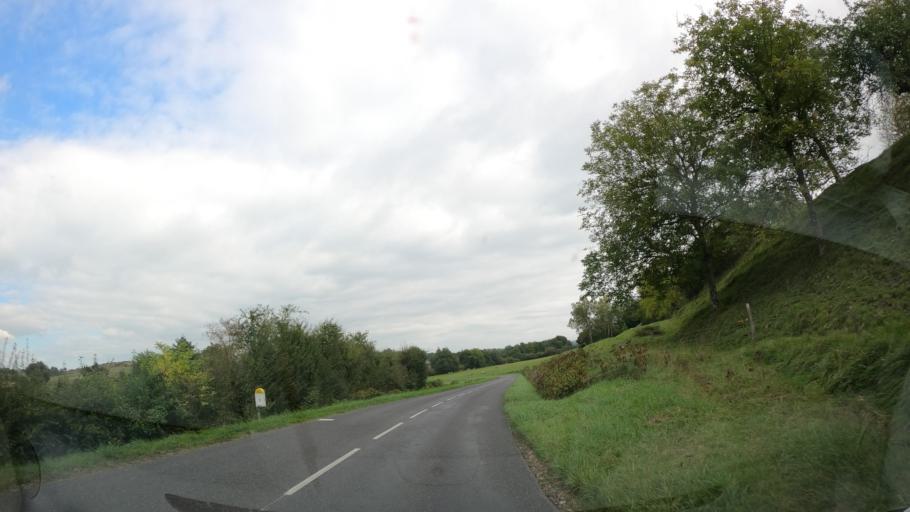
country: FR
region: Auvergne
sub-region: Departement de l'Allier
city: Lapalisse
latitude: 46.3287
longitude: 3.6109
